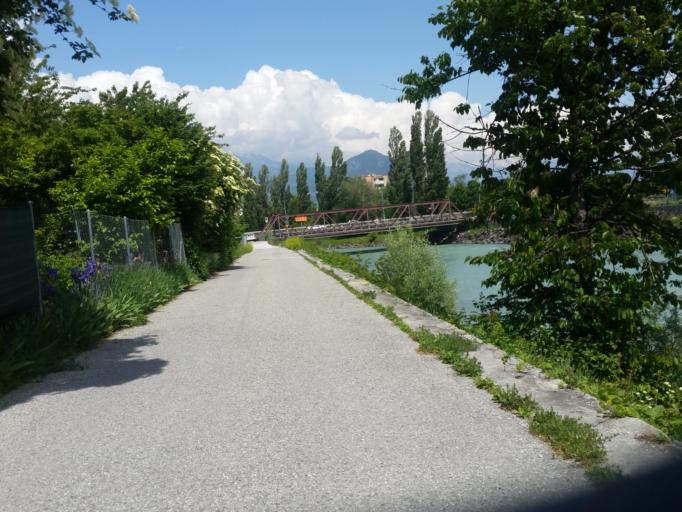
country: CH
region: Valais
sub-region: Sion District
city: Sitten
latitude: 46.2274
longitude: 7.3680
